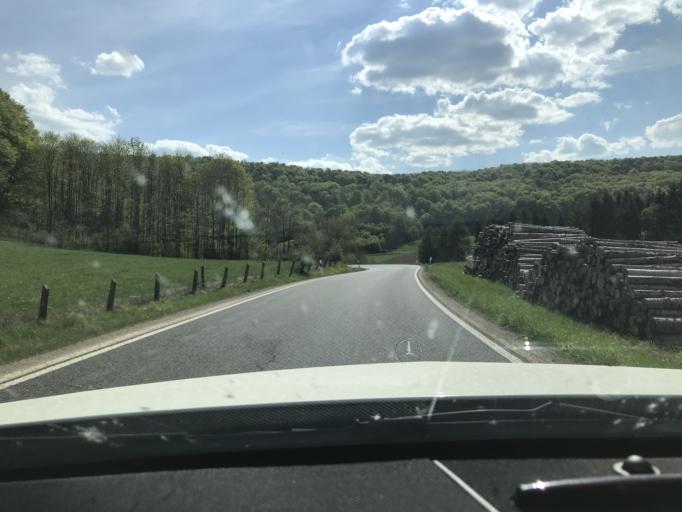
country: DE
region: Hesse
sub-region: Regierungsbezirk Kassel
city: Weissenborn
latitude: 51.1183
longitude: 10.0945
